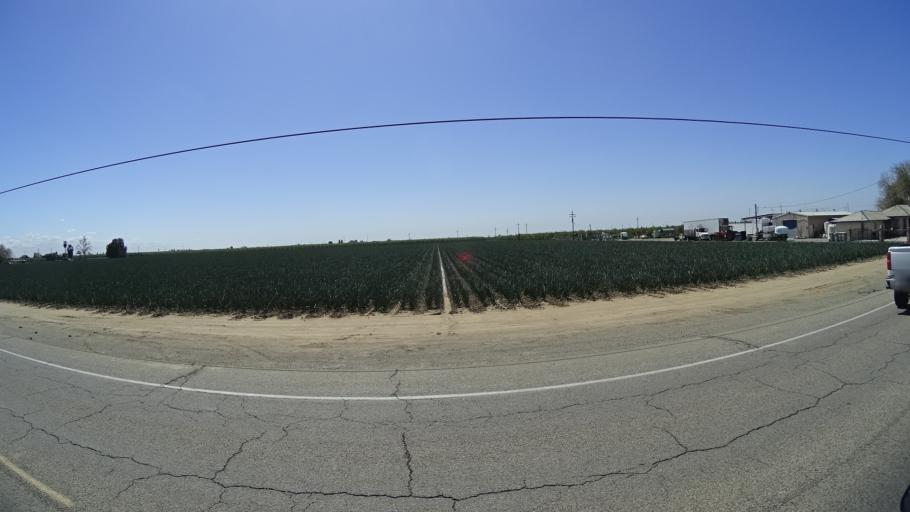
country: US
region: California
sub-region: Fresno County
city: West Park
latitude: 36.7066
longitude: -119.8758
